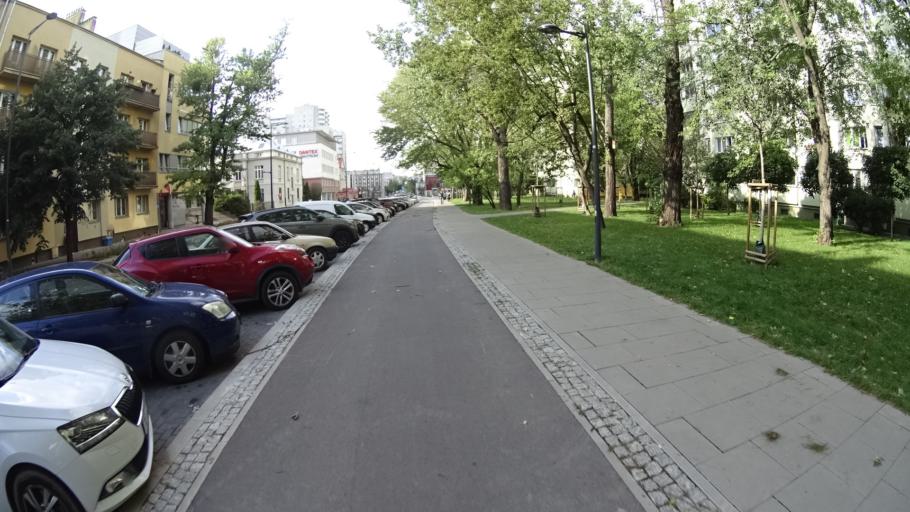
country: PL
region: Masovian Voivodeship
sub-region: Warszawa
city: Ochota
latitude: 52.2305
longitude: 20.9669
